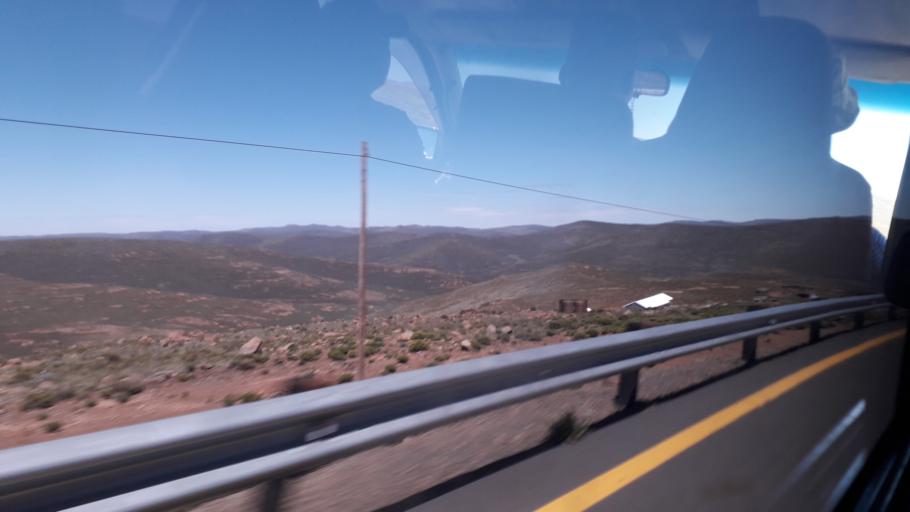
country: LS
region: Mokhotlong
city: Mokhotlong
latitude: -29.0172
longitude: 28.8482
